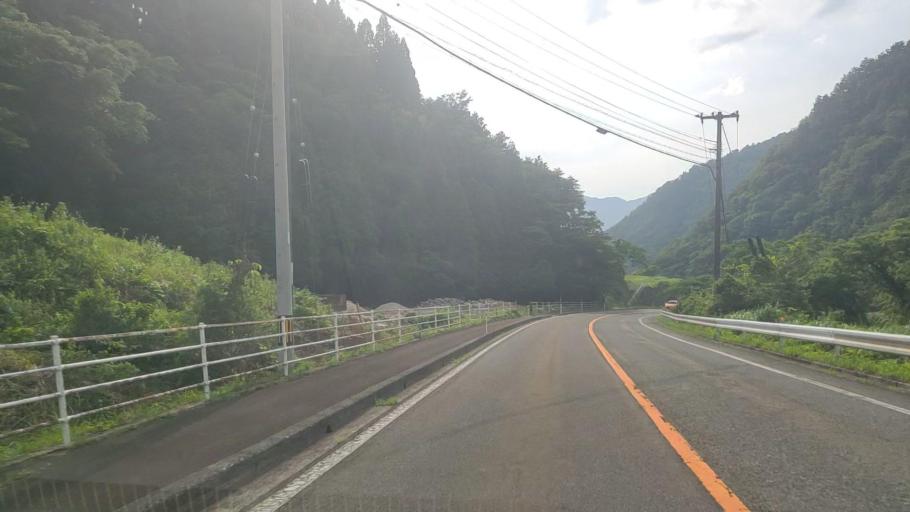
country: JP
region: Tottori
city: Kurayoshi
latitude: 35.3171
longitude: 133.8551
